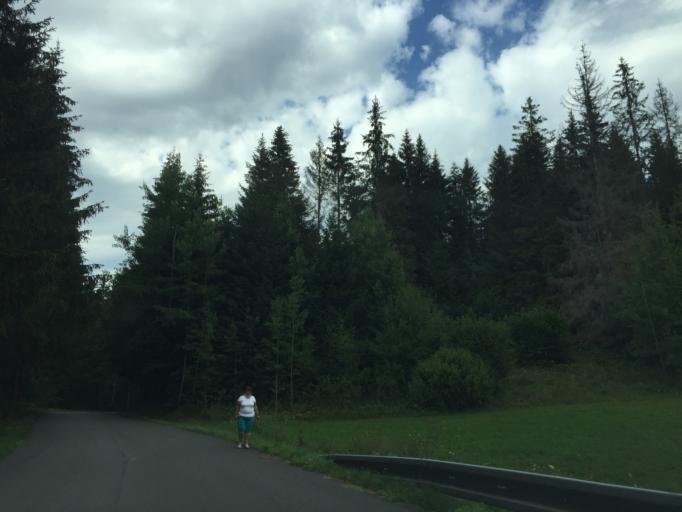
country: SK
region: Zilinsky
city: Namestovo
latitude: 49.4155
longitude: 19.3326
